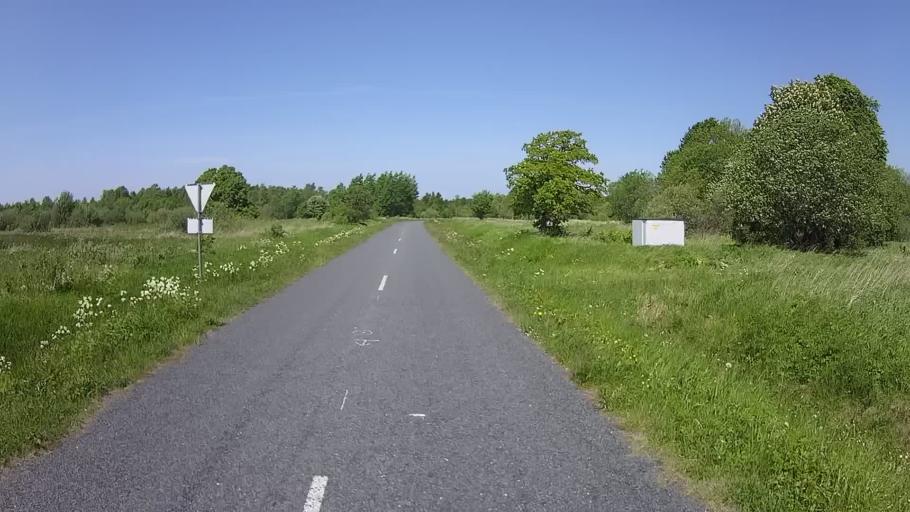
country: LV
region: Dundaga
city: Dundaga
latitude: 57.9364
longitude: 22.0930
